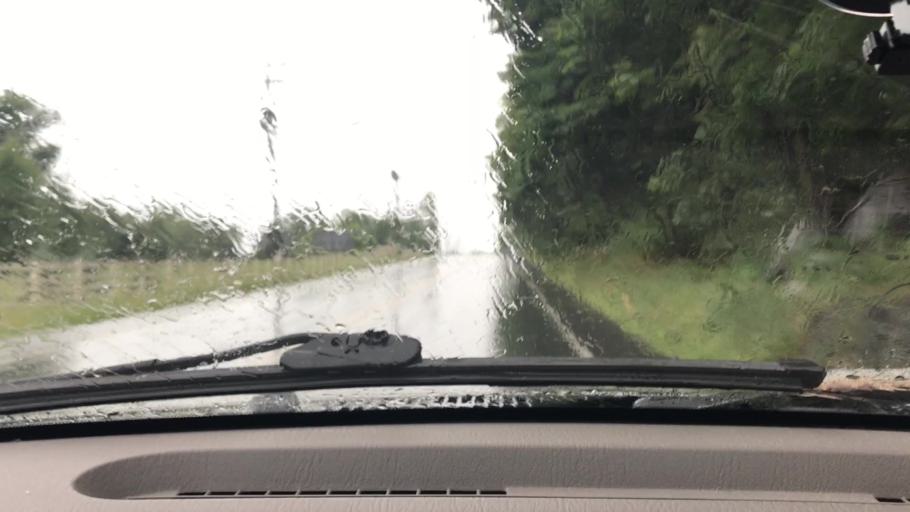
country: US
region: Pennsylvania
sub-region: Lancaster County
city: Elizabethtown
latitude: 40.1589
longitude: -76.6207
